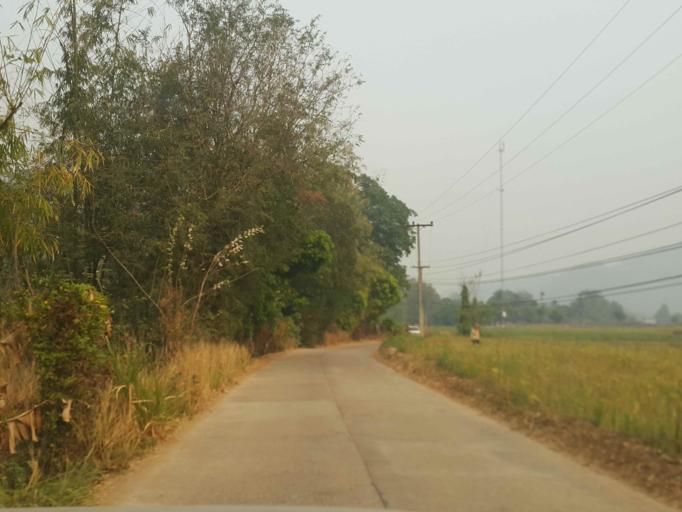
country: TH
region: Chiang Mai
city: Mae Taeng
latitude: 19.2199
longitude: 98.8486
